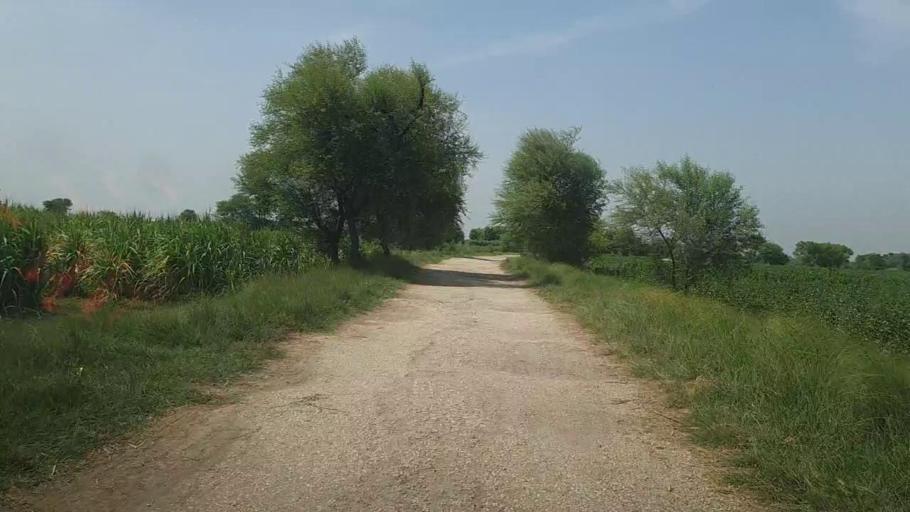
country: PK
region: Sindh
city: Ubauro
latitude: 28.1728
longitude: 69.8156
